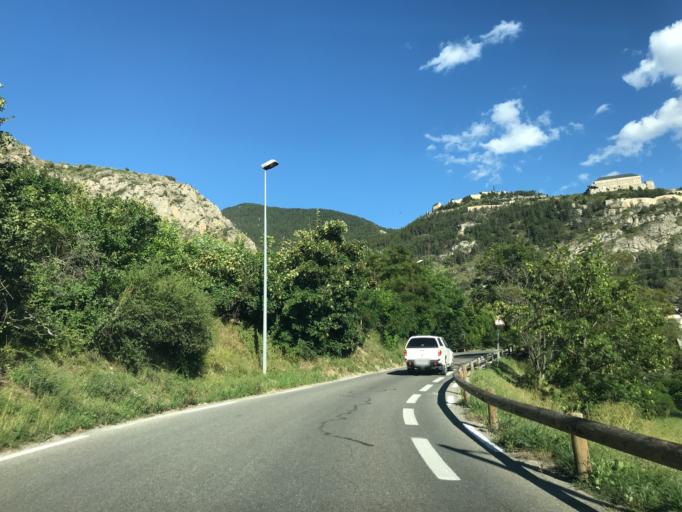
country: FR
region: Provence-Alpes-Cote d'Azur
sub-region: Departement des Hautes-Alpes
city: Briancon
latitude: 44.8931
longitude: 6.6440
